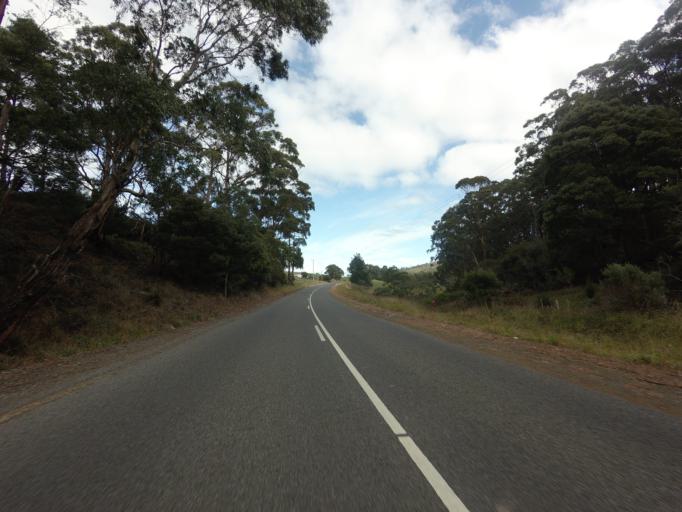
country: AU
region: Tasmania
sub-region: Clarence
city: Sandford
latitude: -43.0786
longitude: 147.7464
